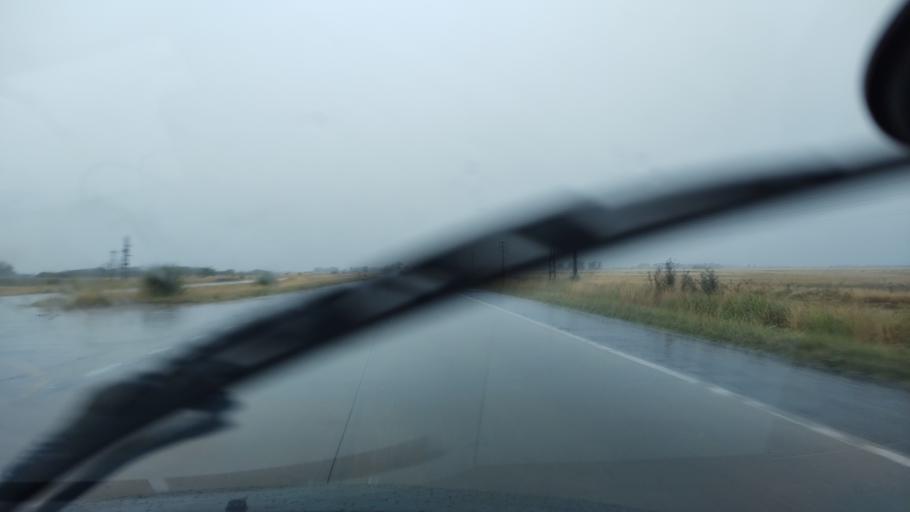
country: AR
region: Buenos Aires
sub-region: Partido de San Vicente
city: San Vicente
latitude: -35.0723
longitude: -58.5340
